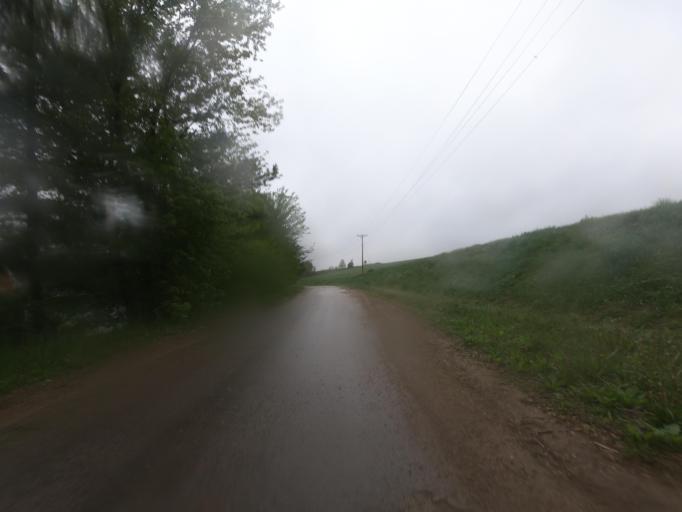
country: US
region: Wisconsin
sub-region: Grant County
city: Hazel Green
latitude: 42.5098
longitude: -90.4628
